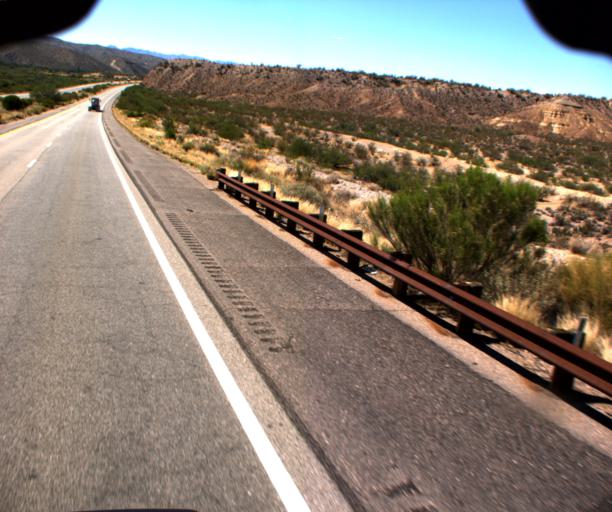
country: US
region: Arizona
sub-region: Yavapai County
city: Bagdad
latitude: 34.6374
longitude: -113.5577
